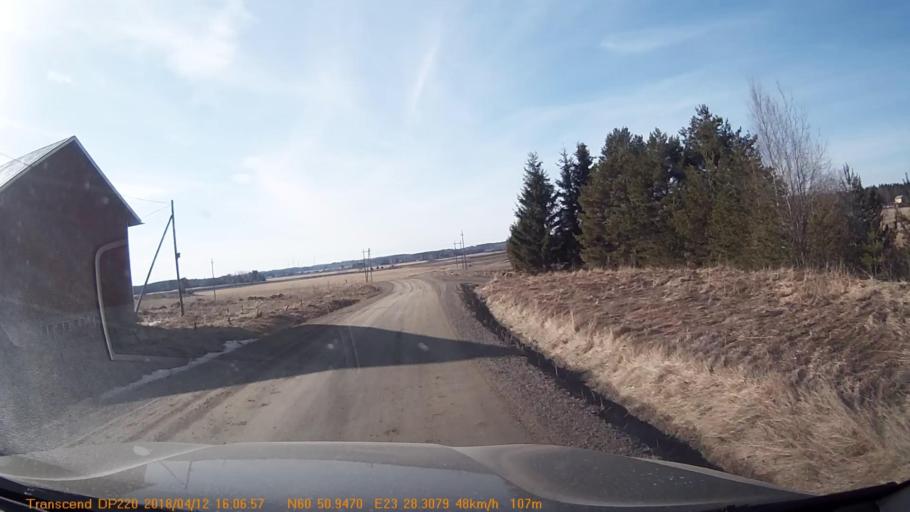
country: FI
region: Haeme
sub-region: Forssa
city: Jokioinen
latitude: 60.8492
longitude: 23.4715
